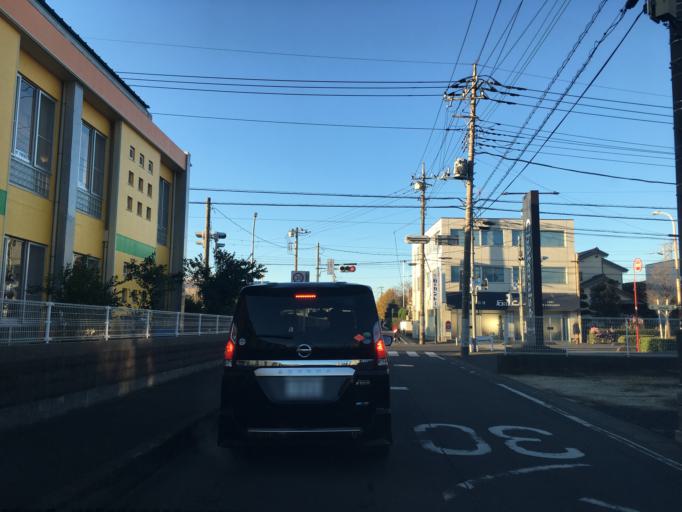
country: JP
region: Saitama
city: Sayama
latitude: 35.8243
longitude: 139.3967
